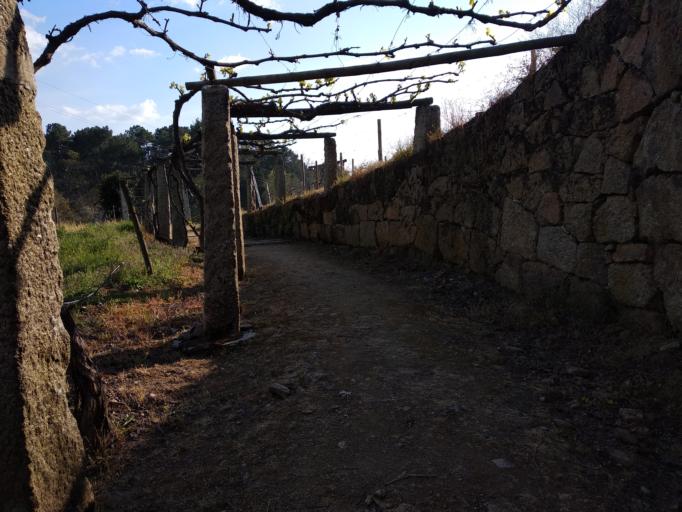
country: PT
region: Vila Real
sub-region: Vila Real
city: Vila Real
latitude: 41.2954
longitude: -7.7130
